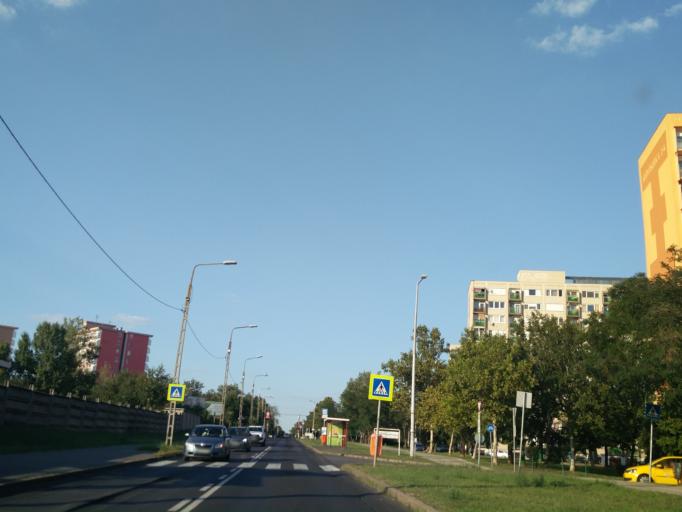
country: HU
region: Budapest
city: Budapest X. keruelet
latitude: 47.4718
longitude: 19.1593
